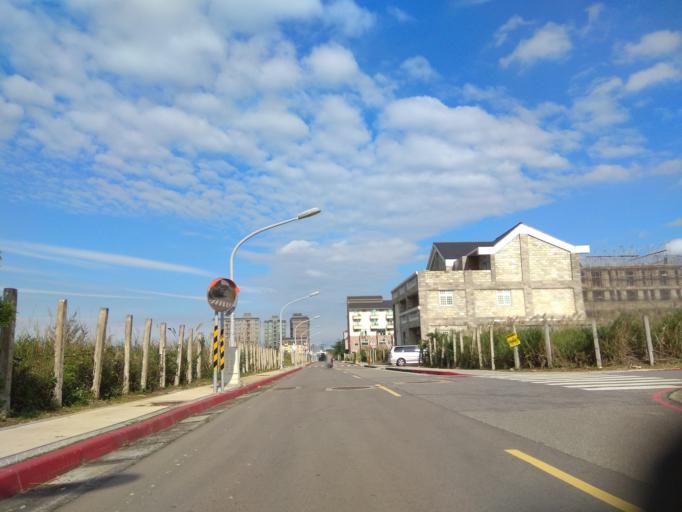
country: TW
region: Taiwan
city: Taoyuan City
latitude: 25.0514
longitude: 121.1757
